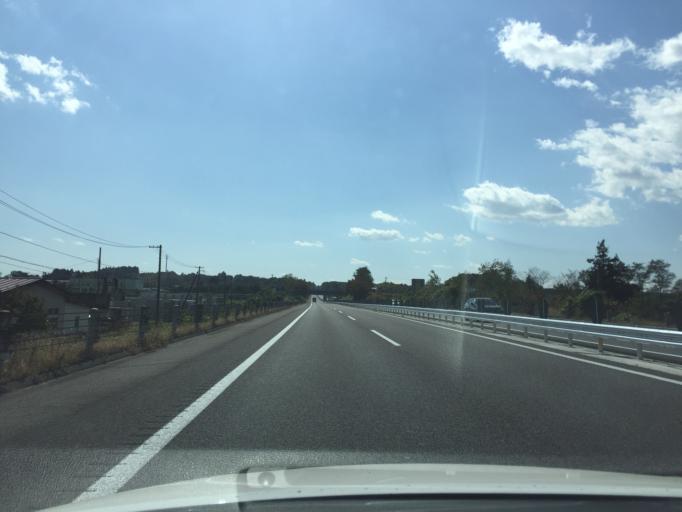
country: JP
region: Fukushima
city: Sukagawa
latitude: 37.2471
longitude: 140.3310
